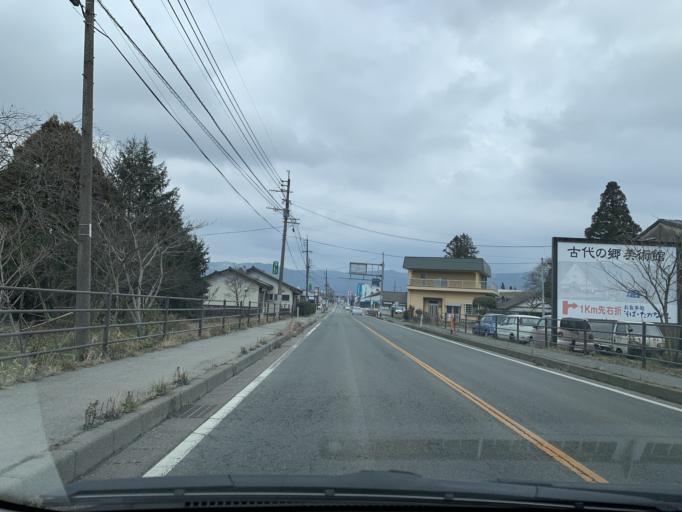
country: JP
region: Kumamoto
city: Aso
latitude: 32.9382
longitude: 131.1038
